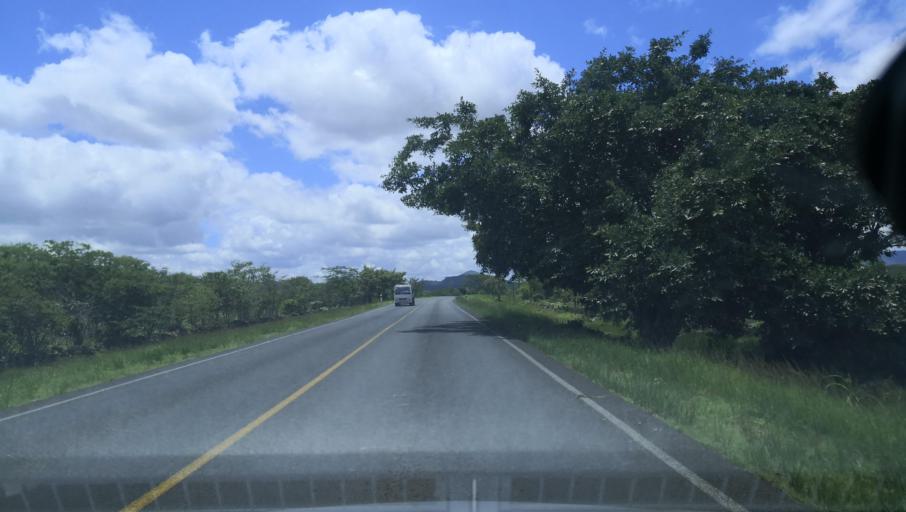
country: NI
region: Esteli
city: Esteli
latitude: 13.2195
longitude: -86.3797
